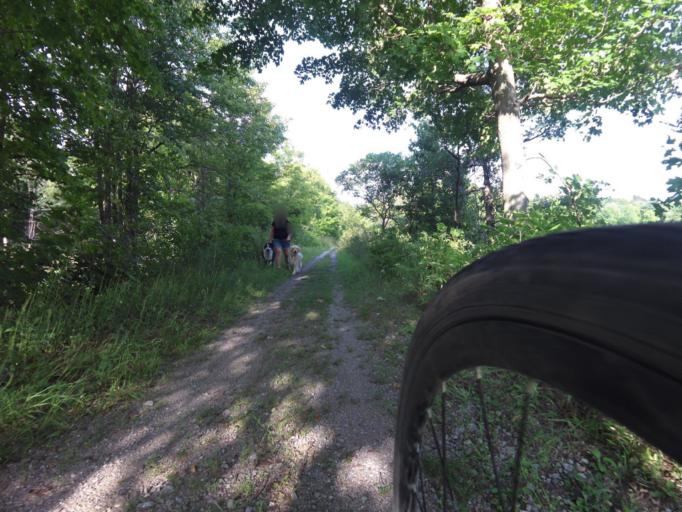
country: CA
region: Ontario
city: Kingston
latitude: 44.4691
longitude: -76.5024
